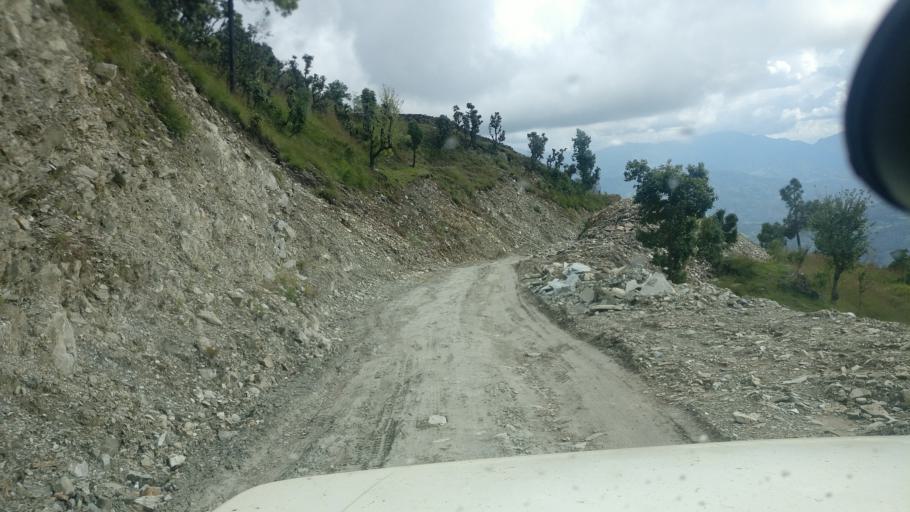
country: NP
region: Western Region
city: Baglung
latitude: 28.2833
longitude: 83.6387
